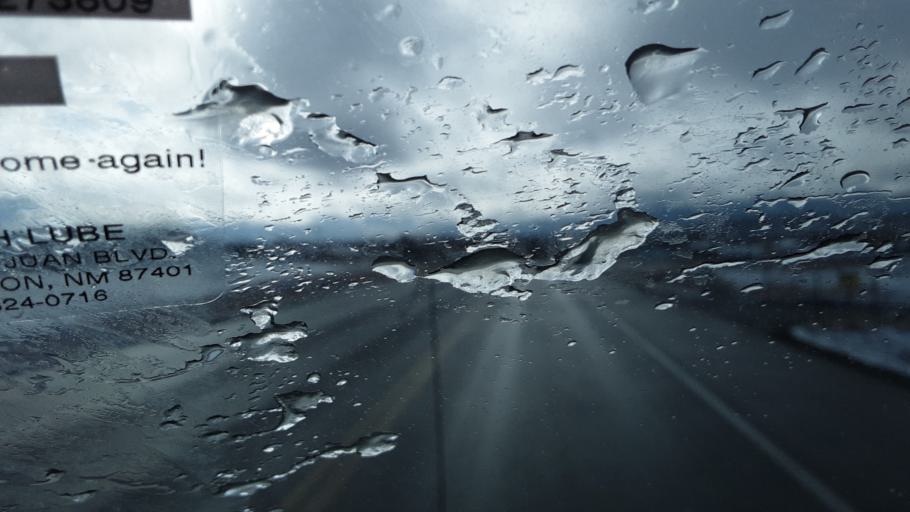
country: US
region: Colorado
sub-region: La Plata County
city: Bayfield
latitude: 37.2341
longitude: -107.5885
